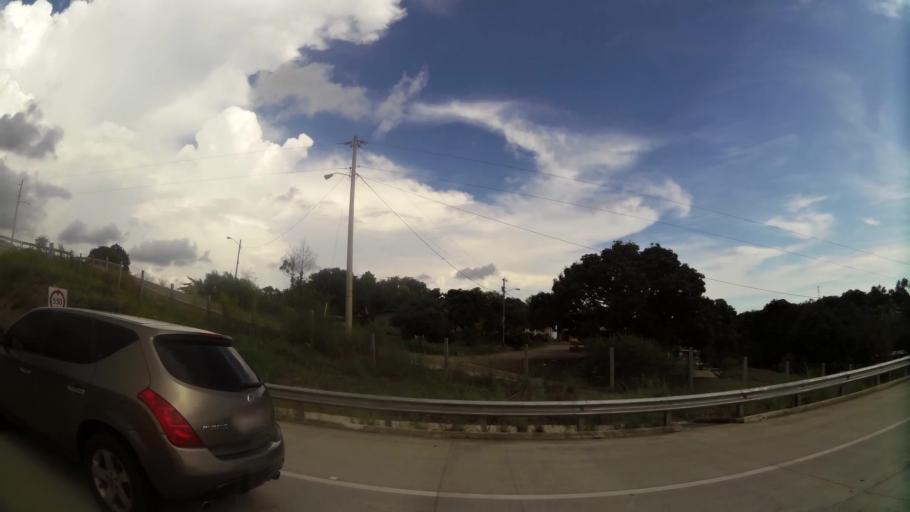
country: PA
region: Panama
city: Tocumen
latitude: 9.0971
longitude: -79.4212
